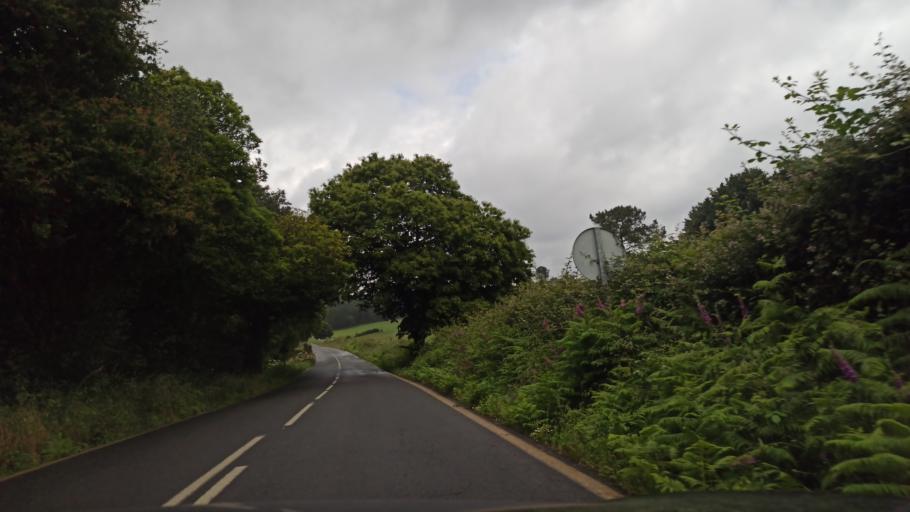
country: ES
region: Galicia
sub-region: Provincia da Coruna
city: Santiso
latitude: 42.7793
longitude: -8.0370
